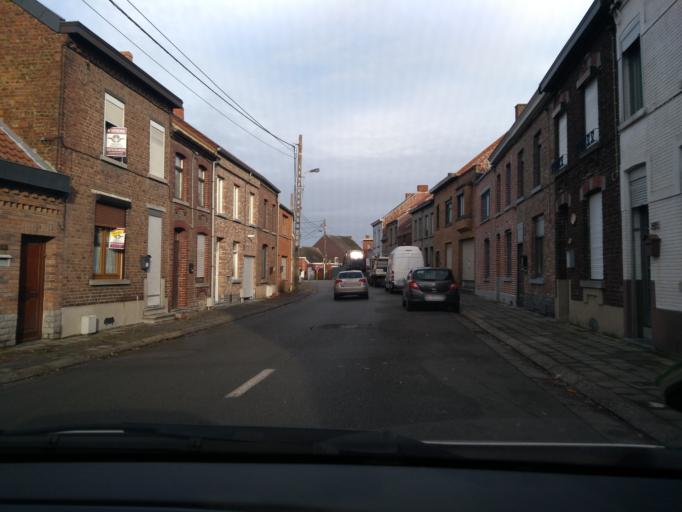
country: BE
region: Wallonia
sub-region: Province du Hainaut
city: Frameries
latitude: 50.4024
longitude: 3.8827
